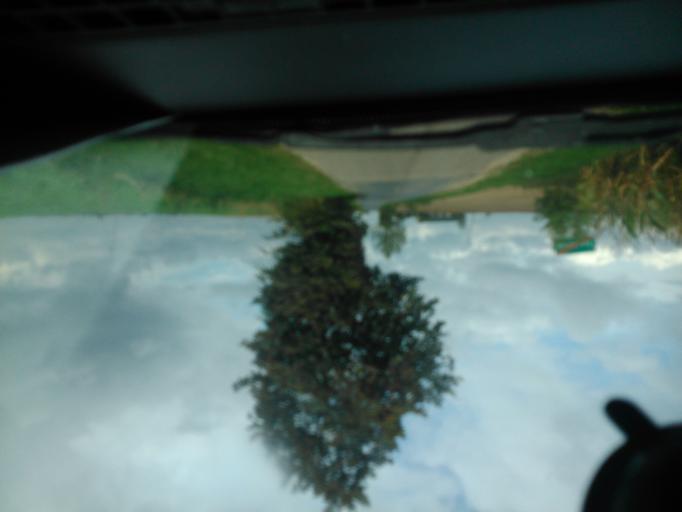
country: PL
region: Kujawsko-Pomorskie
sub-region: Powiat brodnicki
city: Swiedziebnia
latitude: 53.2013
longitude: 19.4758
